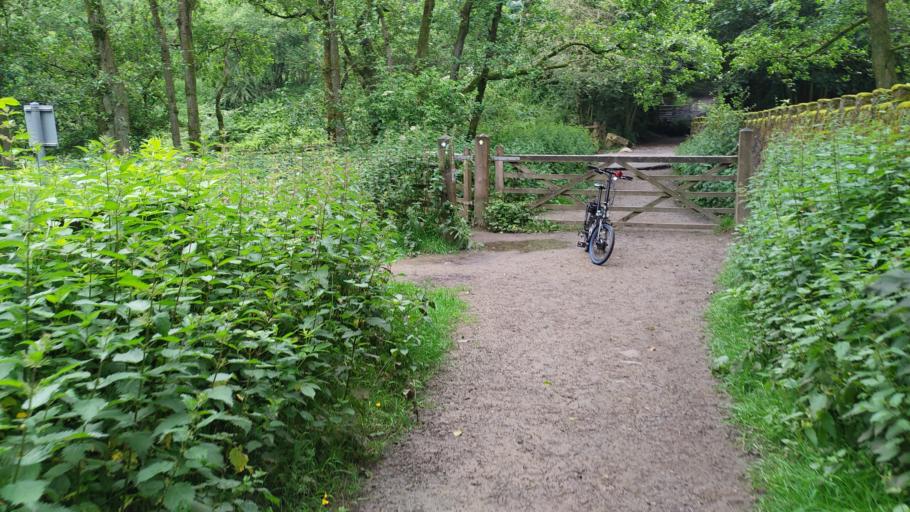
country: GB
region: England
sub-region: Lancashire
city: Chorley
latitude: 53.6839
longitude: -2.5695
